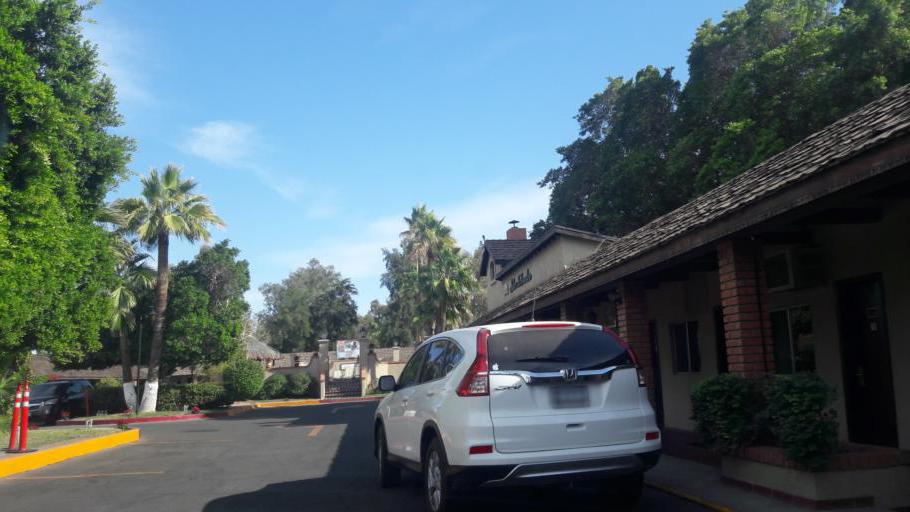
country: MX
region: Baja California
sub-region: Mexicali
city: Mexicali
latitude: 32.6562
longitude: -115.4521
